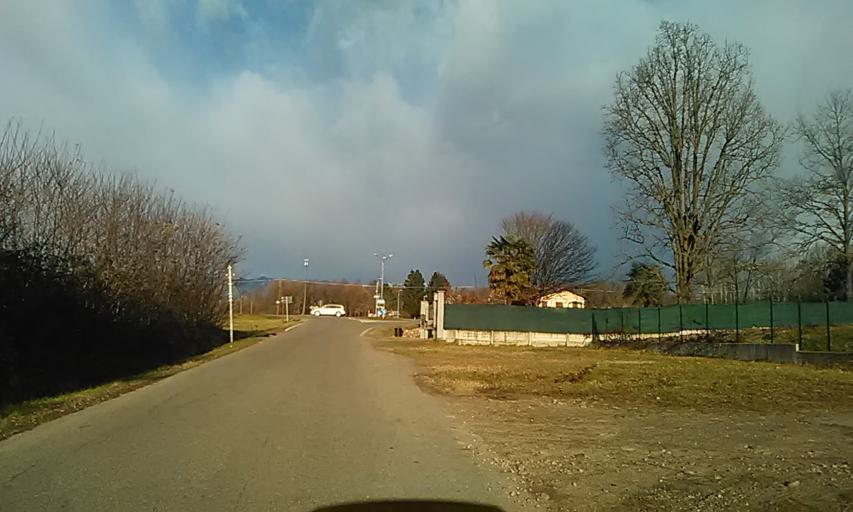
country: IT
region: Piedmont
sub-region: Provincia di Biella
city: Brusnengo
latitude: 45.5803
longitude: 8.2627
